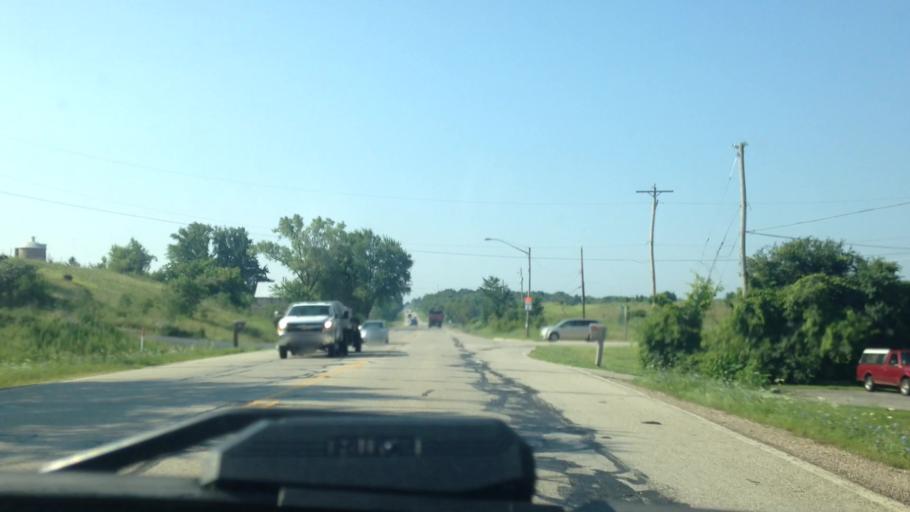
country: US
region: Wisconsin
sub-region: Waukesha County
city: Merton
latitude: 43.1857
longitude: -88.2619
